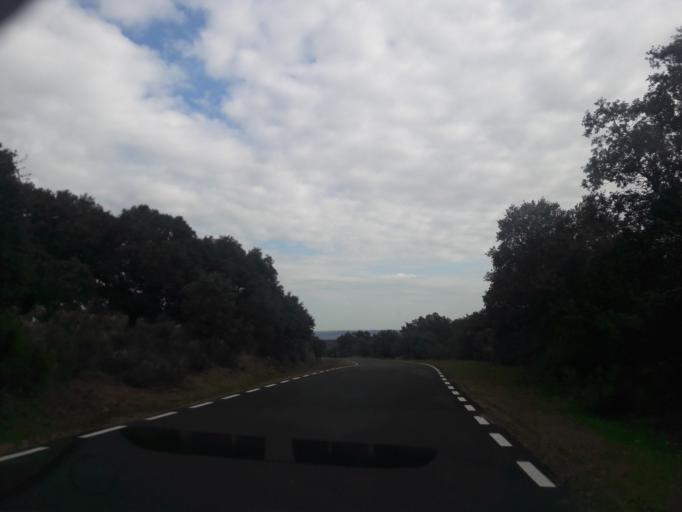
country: ES
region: Castille and Leon
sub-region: Provincia de Salamanca
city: Pastores
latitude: 40.5190
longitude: -6.5268
